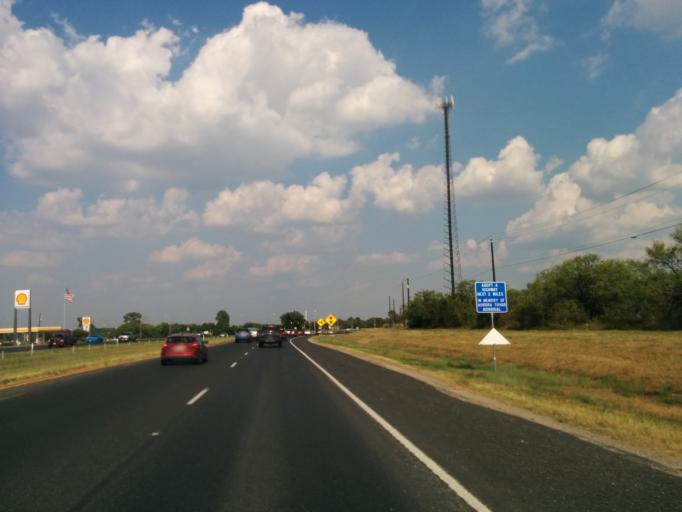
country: US
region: Texas
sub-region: Bexar County
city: Elmendorf
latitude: 29.3077
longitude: -98.3935
